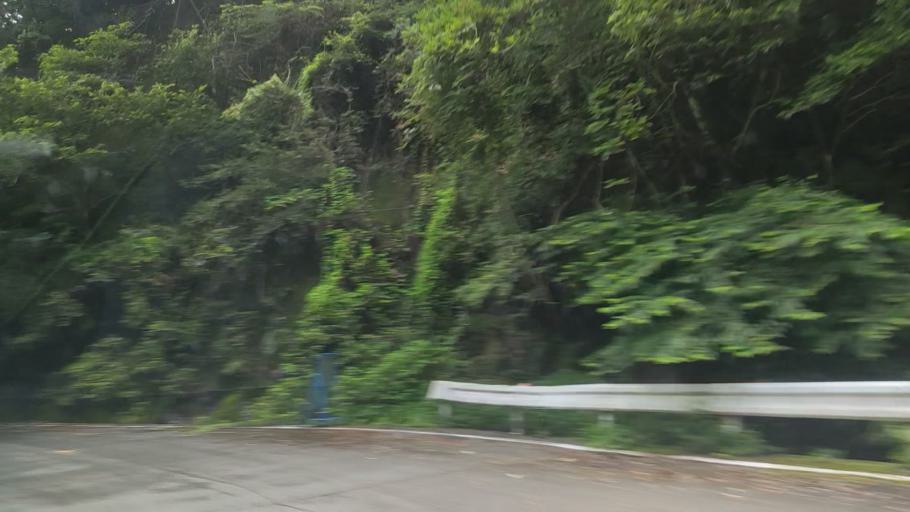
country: JP
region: Shizuoka
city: Fujinomiya
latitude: 35.2143
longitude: 138.5259
